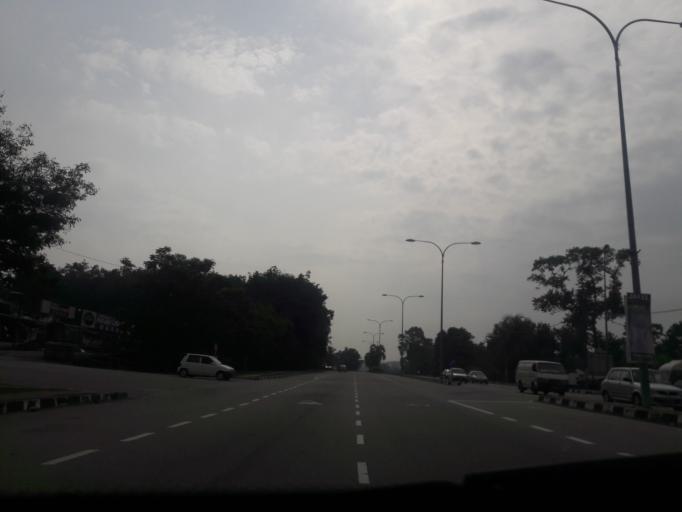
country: MY
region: Kedah
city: Kulim
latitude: 5.3533
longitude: 100.5332
